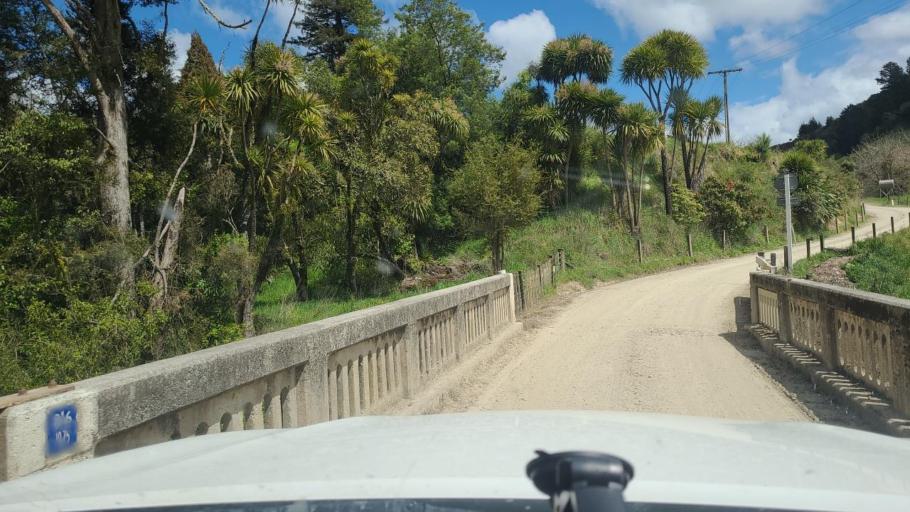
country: NZ
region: Hawke's Bay
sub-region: Wairoa District
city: Wairoa
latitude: -38.8478
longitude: 177.6814
